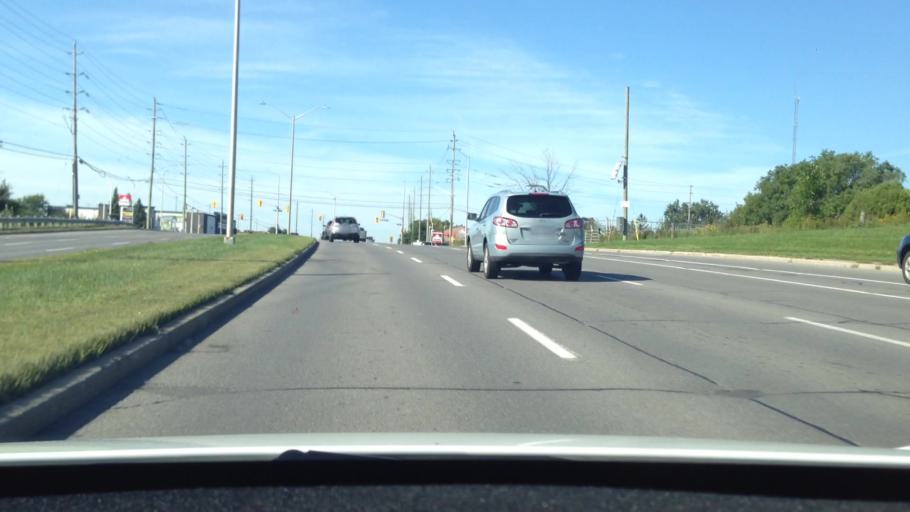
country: CA
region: Ontario
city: Ottawa
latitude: 45.4205
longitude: -75.5942
